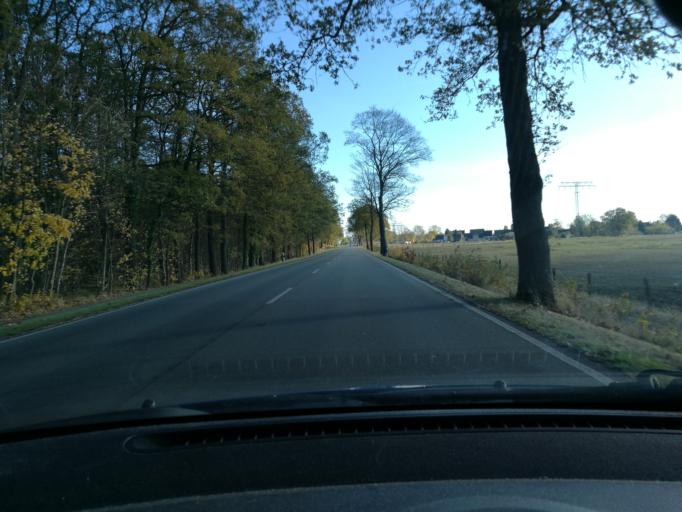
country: DE
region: Brandenburg
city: Perleberg
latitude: 53.1057
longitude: 11.8264
